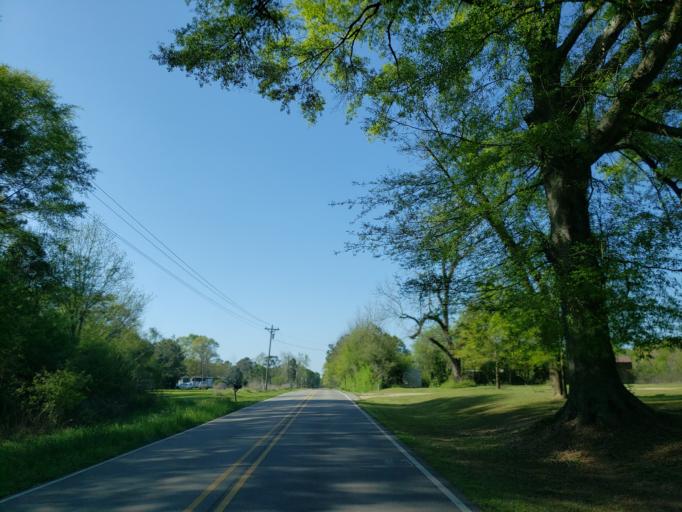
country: US
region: Mississippi
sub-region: Jones County
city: Ellisville
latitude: 31.5733
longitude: -89.3711
